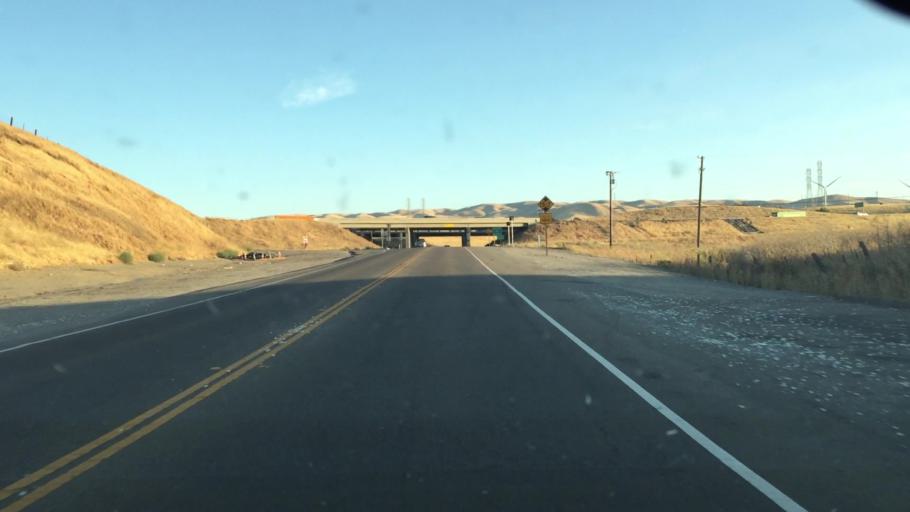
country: US
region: California
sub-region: San Joaquin County
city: Mountain House
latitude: 37.7424
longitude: -121.5853
